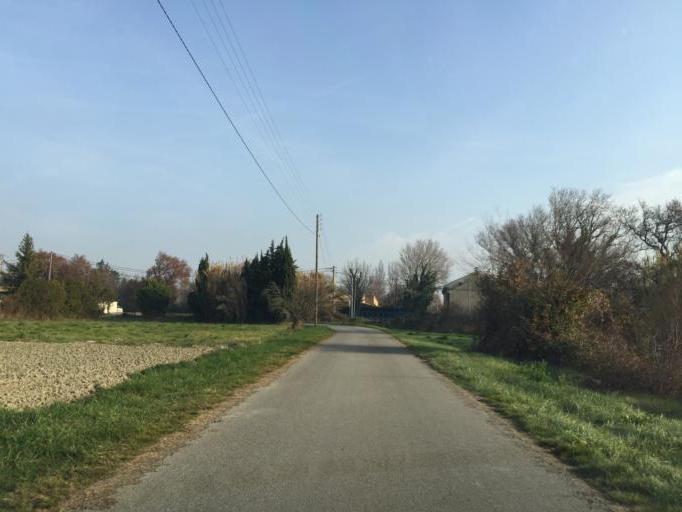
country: FR
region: Provence-Alpes-Cote d'Azur
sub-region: Departement du Vaucluse
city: Jonquieres
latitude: 44.1250
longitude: 4.8965
